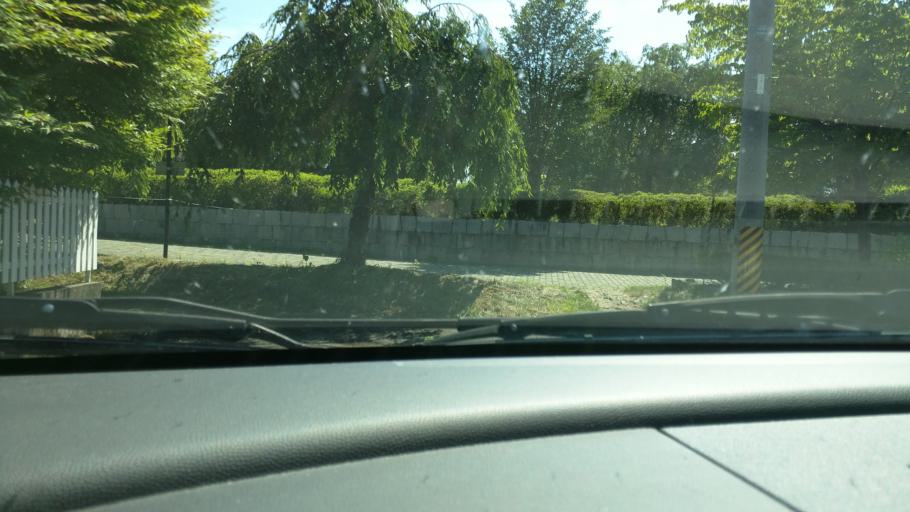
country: JP
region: Fukushima
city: Kitakata
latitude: 37.6651
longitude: 139.8708
